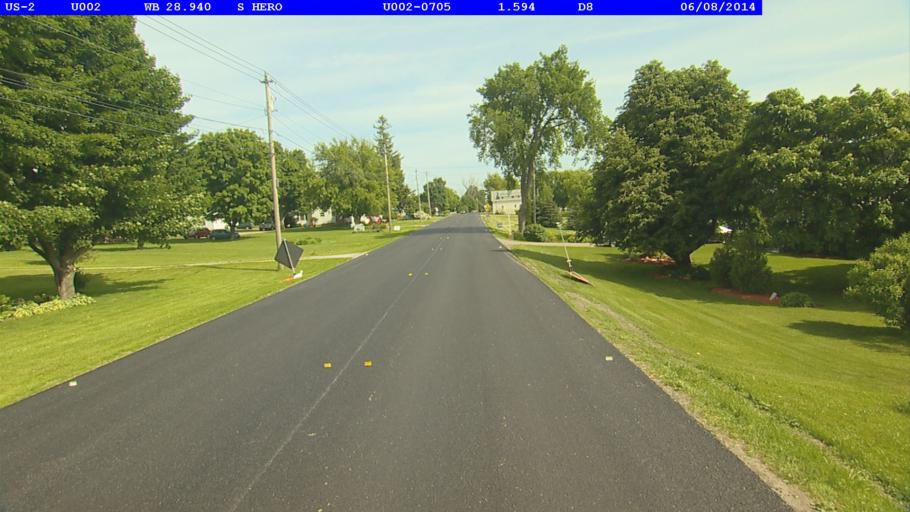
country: US
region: New York
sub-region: Clinton County
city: Cumberland Head
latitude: 44.6582
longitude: -73.3214
